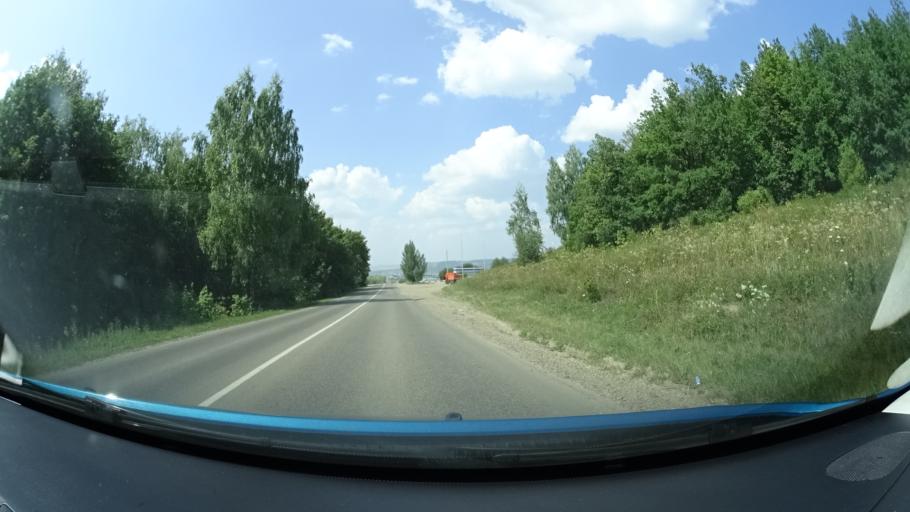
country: RU
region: Bashkortostan
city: Oktyabr'skiy
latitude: 54.4774
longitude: 53.5708
